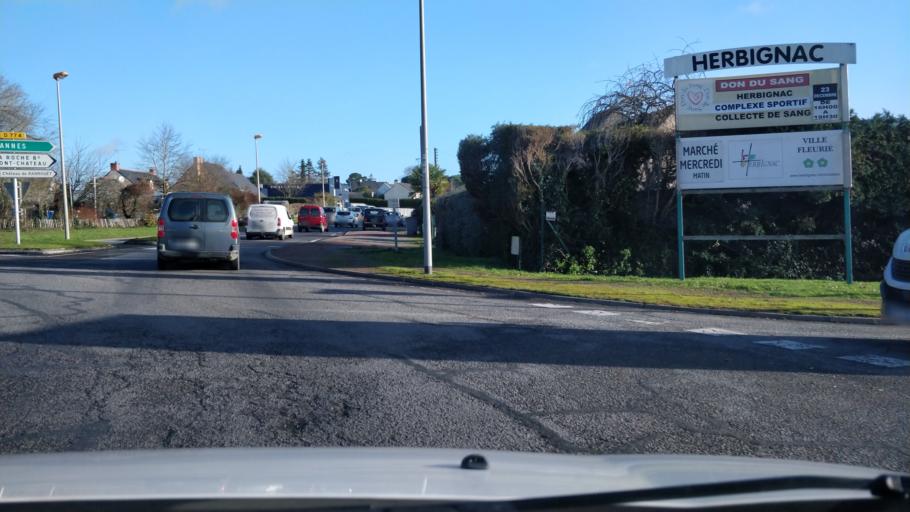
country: FR
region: Pays de la Loire
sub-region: Departement de la Loire-Atlantique
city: Herbignac
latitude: 47.4446
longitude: -2.3220
